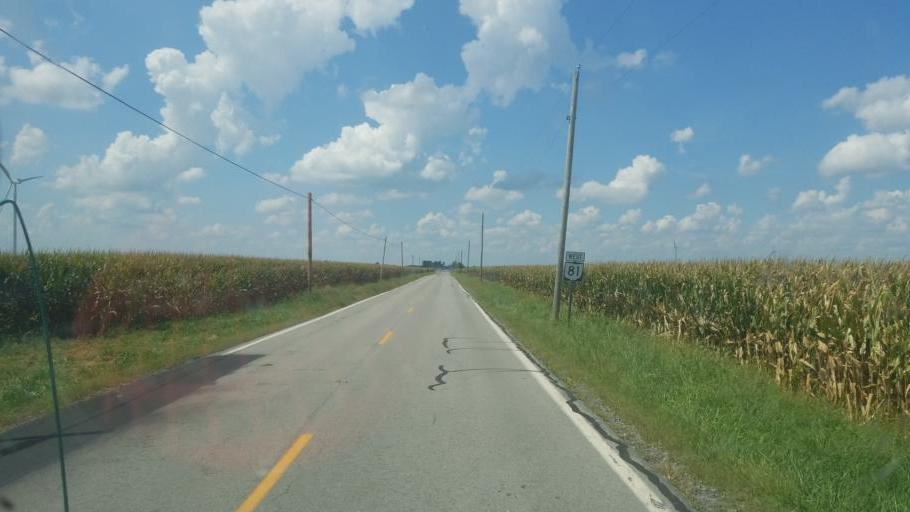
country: US
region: Ohio
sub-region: Hardin County
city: Ada
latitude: 40.7763
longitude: -83.7289
